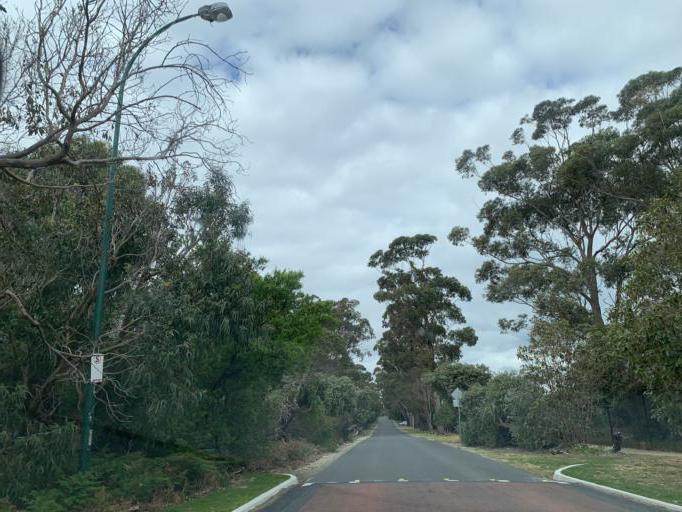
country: AU
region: Victoria
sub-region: Bayside
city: Black Rock
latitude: -37.9677
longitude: 145.0243
